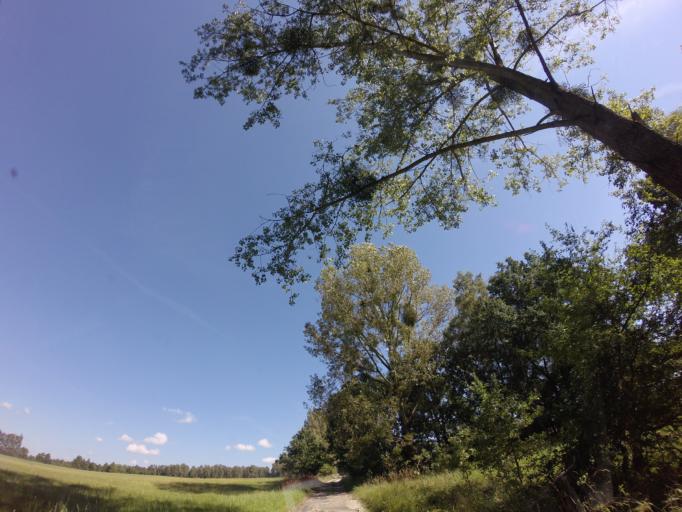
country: PL
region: West Pomeranian Voivodeship
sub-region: Powiat choszczenski
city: Recz
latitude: 53.1626
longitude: 15.5719
